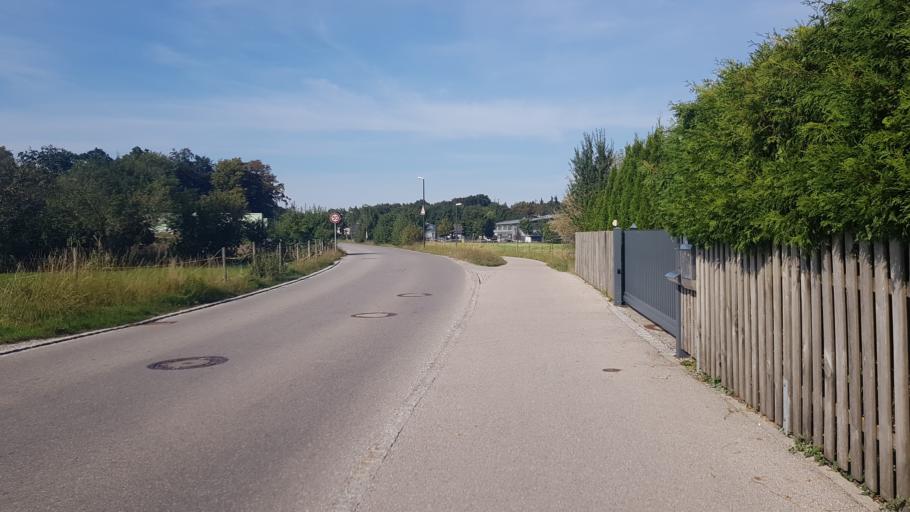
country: DE
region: Bavaria
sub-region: Upper Bavaria
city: Wessling
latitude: 48.0788
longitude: 11.2658
